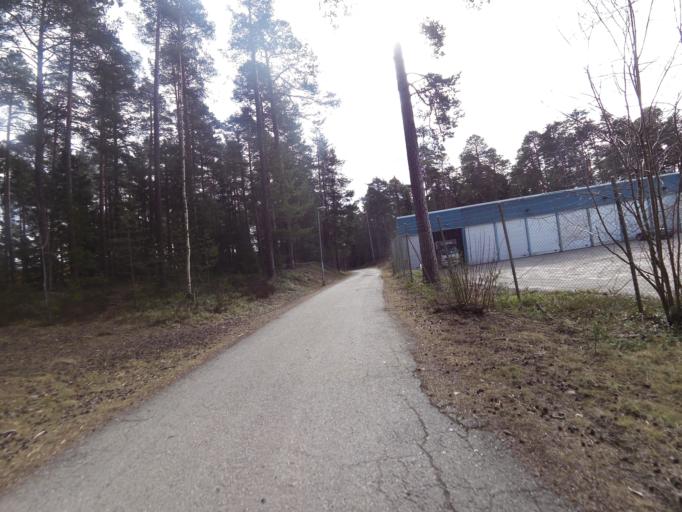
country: SE
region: Gaevleborg
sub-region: Gavle Kommun
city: Gavle
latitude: 60.6880
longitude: 17.1282
